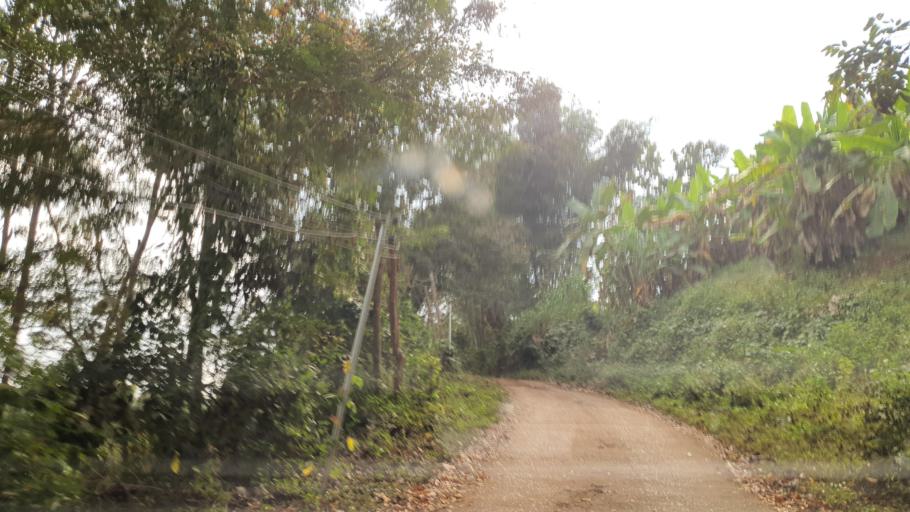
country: TH
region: Chiang Mai
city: Mae Wang
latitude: 18.6687
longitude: 98.6538
